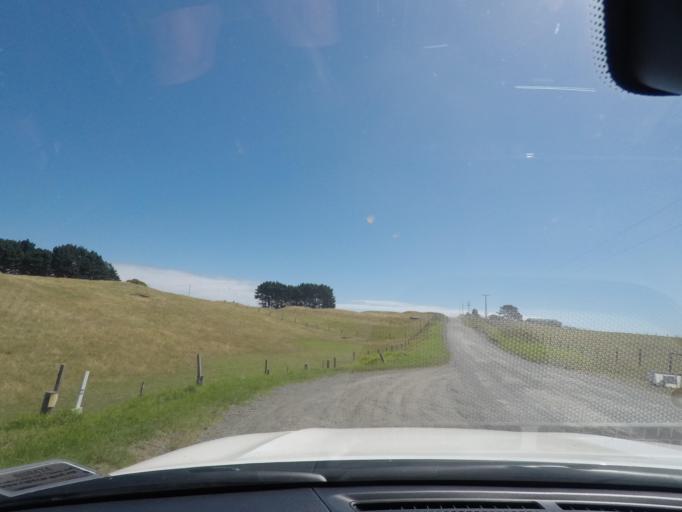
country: NZ
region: Auckland
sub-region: Auckland
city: Parakai
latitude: -36.5840
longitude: 174.2962
